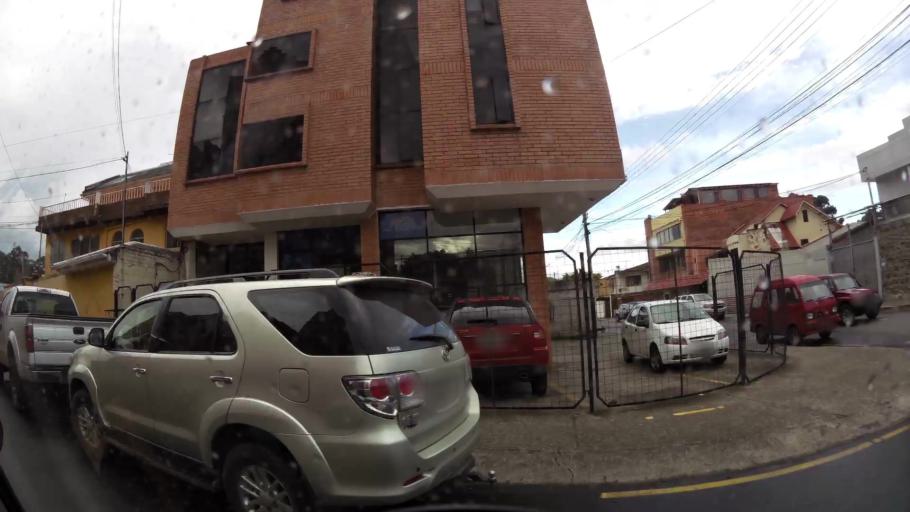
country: EC
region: Azuay
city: Cuenca
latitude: -2.8975
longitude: -79.0187
